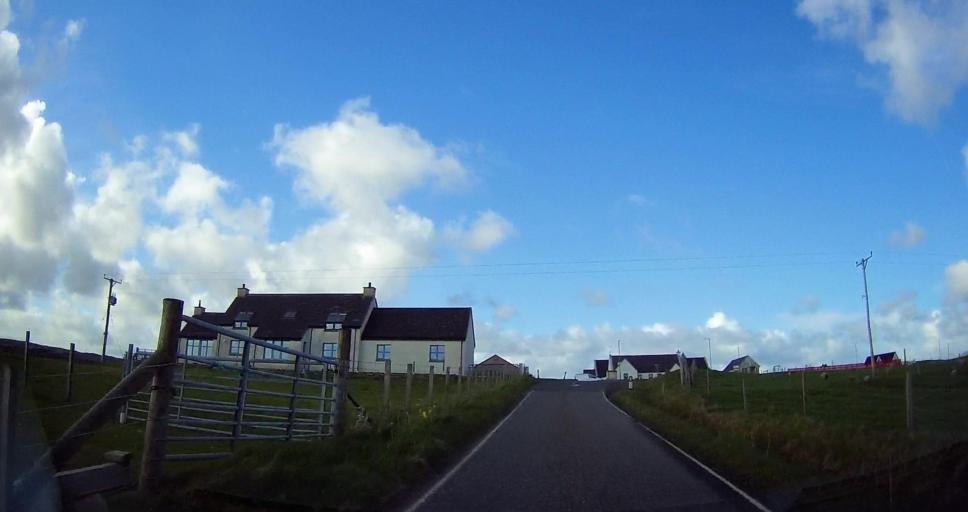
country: GB
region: Scotland
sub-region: Shetland Islands
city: Shetland
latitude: 60.3680
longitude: -1.1409
